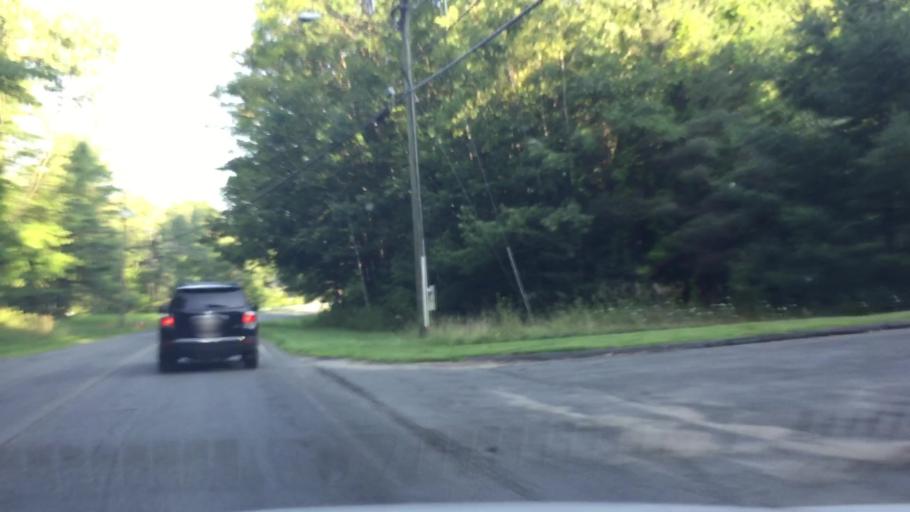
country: US
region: Massachusetts
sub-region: Berkshire County
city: Dalton
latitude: 42.4641
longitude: -73.1913
